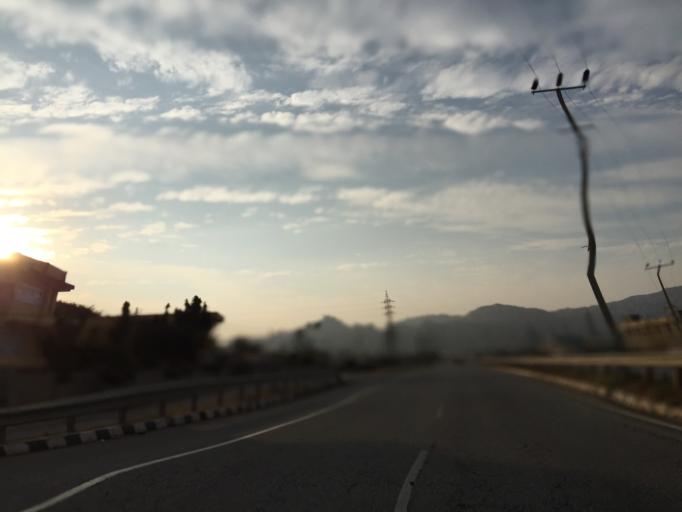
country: IN
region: Karnataka
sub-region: Kolar
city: Kolar
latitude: 13.1228
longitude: 78.1235
